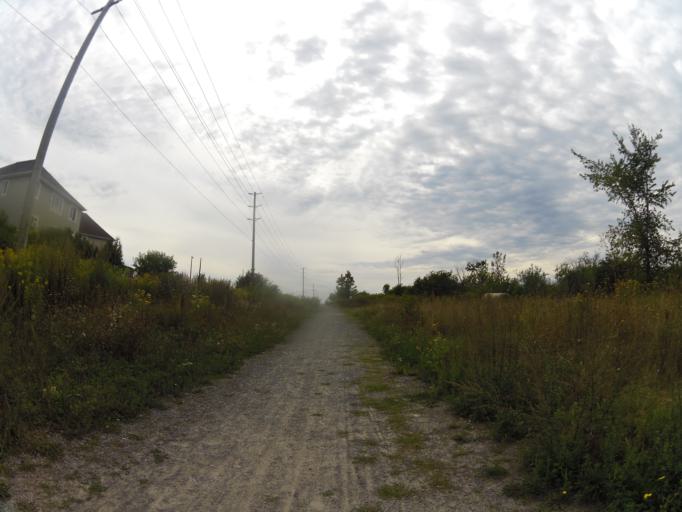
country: CA
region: Ontario
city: Bells Corners
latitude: 45.2811
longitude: -75.9327
